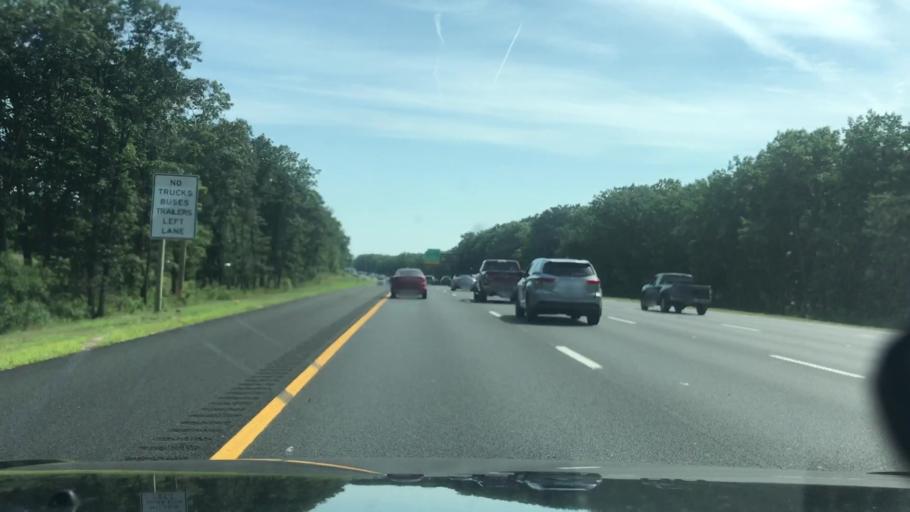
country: US
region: New Jersey
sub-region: Monmouth County
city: Ramtown
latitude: 40.1139
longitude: -74.1323
